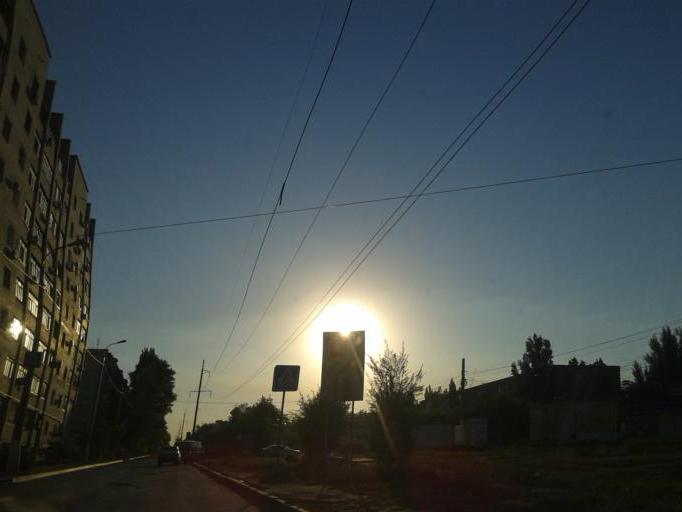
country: RU
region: Volgograd
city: Gorodishche
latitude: 48.7676
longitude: 44.4937
